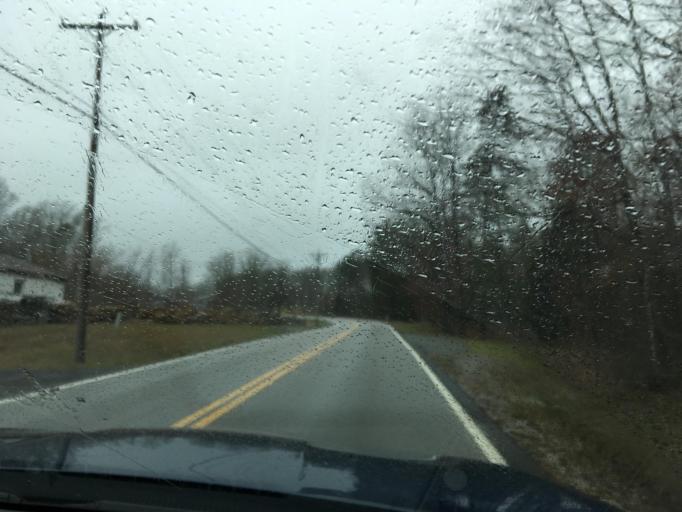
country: US
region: Tennessee
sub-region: Rhea County
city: Spring City
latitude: 35.7627
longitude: -84.8624
